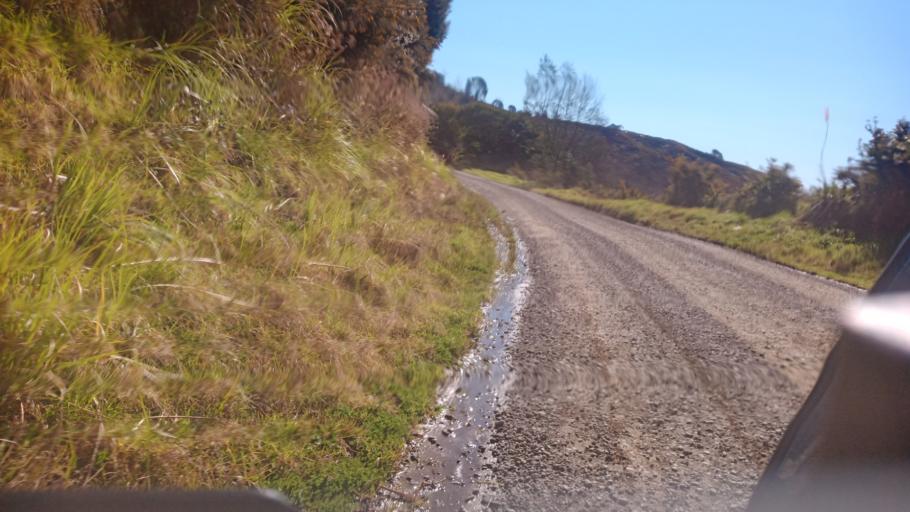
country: NZ
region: Bay of Plenty
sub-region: Opotiki District
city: Opotiki
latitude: -38.0116
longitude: 177.4174
